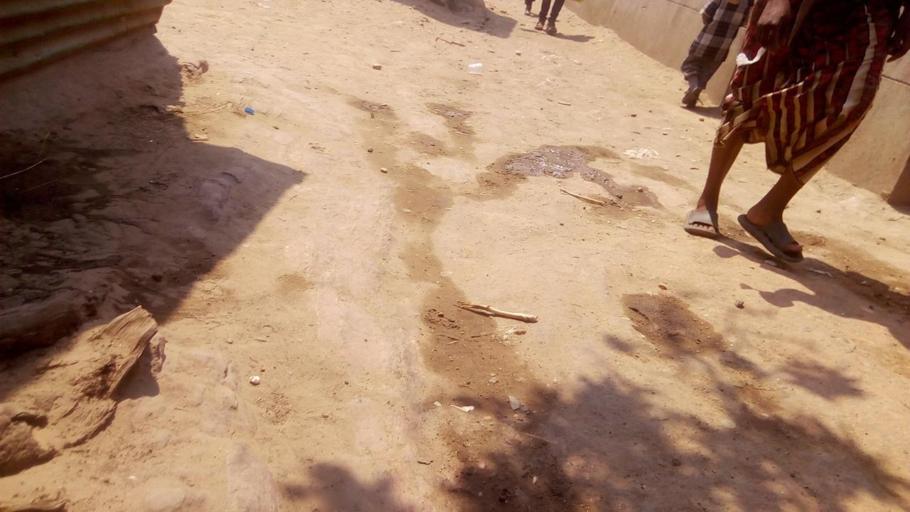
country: ZM
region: Lusaka
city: Lusaka
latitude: -15.3605
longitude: 28.2969
